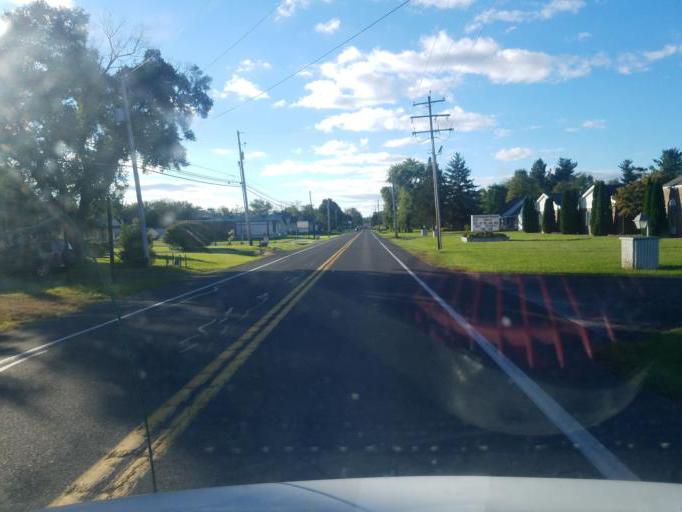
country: US
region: Pennsylvania
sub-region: Adams County
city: Gettysburg
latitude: 39.8566
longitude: -77.2355
